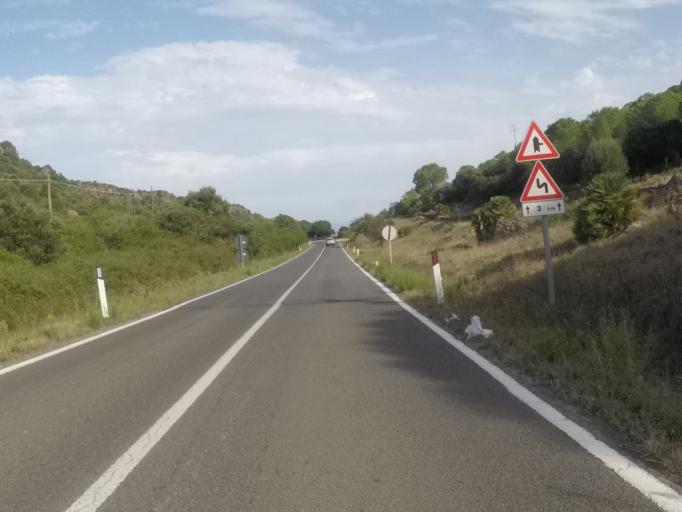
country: IT
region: Sardinia
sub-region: Provincia di Sassari
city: Castelsardo
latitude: 40.8991
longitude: 8.7422
